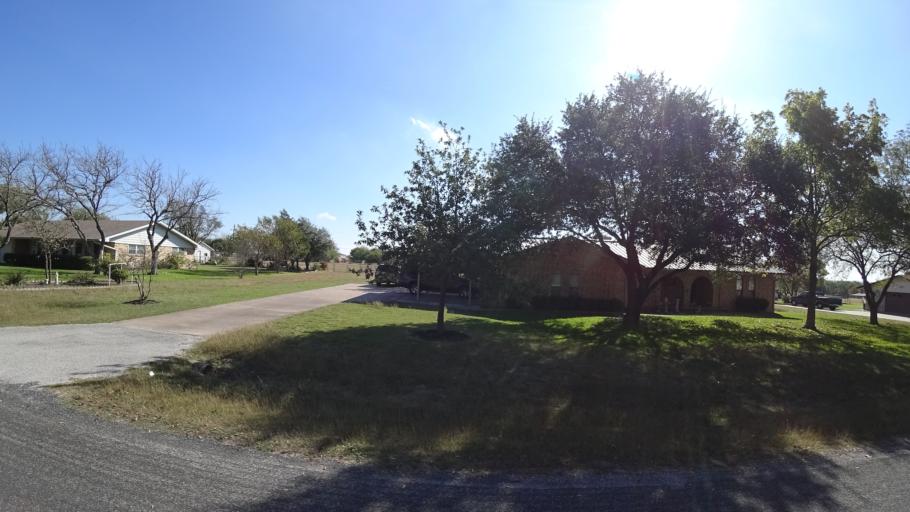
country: US
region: Texas
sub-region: Travis County
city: Windemere
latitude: 30.4417
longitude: -97.6488
